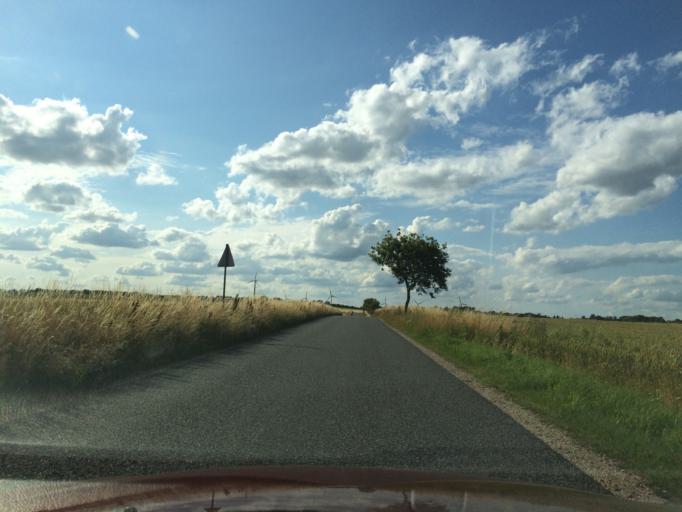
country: DK
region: Central Jutland
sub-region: Silkeborg Kommune
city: Svejbaek
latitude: 56.2459
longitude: 9.7196
